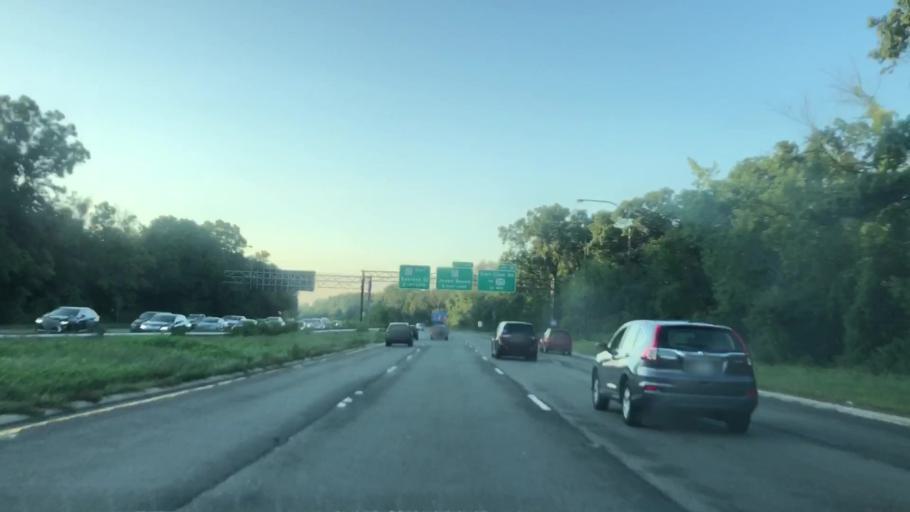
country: US
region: New York
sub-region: Nassau County
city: East Williston
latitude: 40.7654
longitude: -73.6252
